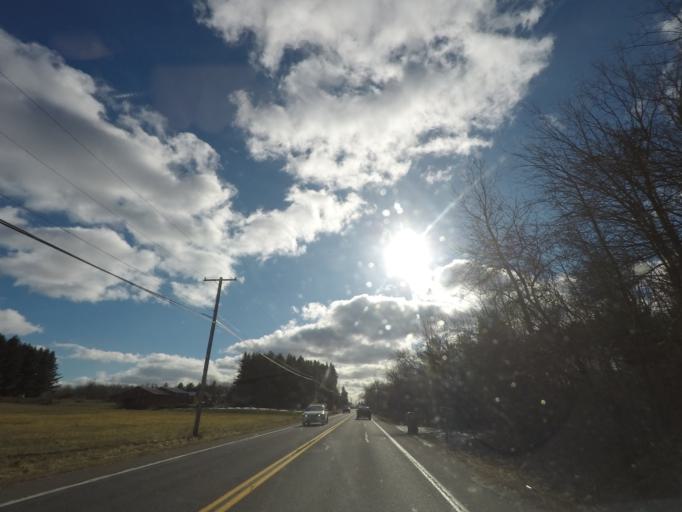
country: US
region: New York
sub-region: Saratoga County
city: Country Knolls
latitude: 42.9166
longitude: -73.8615
